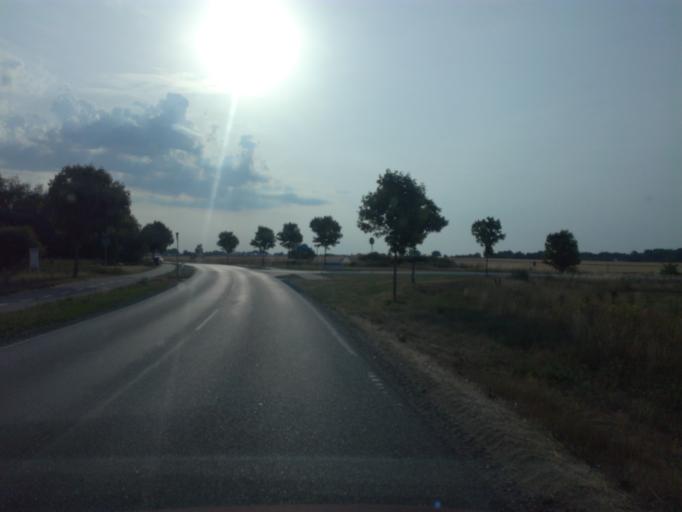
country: DK
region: South Denmark
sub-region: Vejle Kommune
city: Borkop
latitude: 55.6362
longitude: 9.6277
